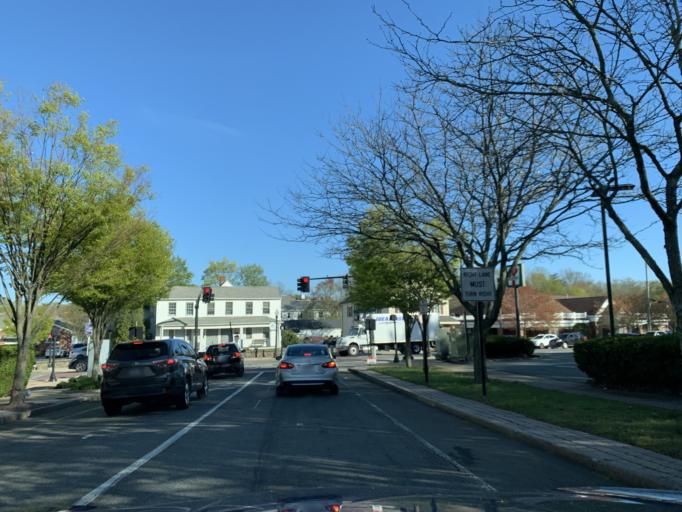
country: US
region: Massachusetts
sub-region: Norfolk County
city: Canton
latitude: 42.1523
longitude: -71.1489
